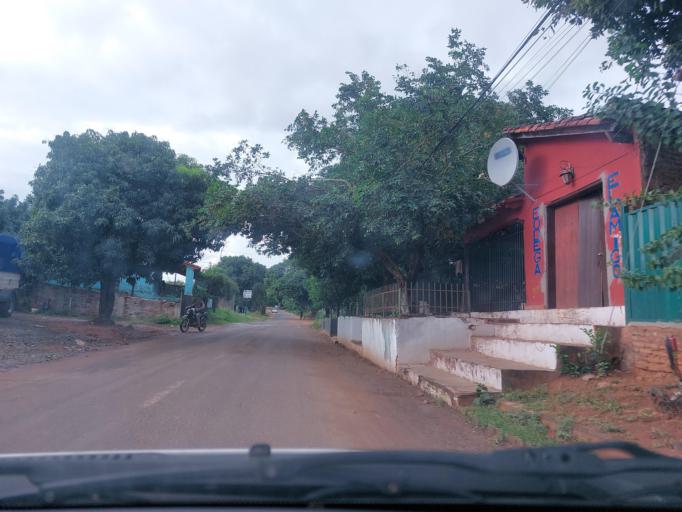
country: PY
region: San Pedro
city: Guayaybi
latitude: -24.6778
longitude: -56.4494
